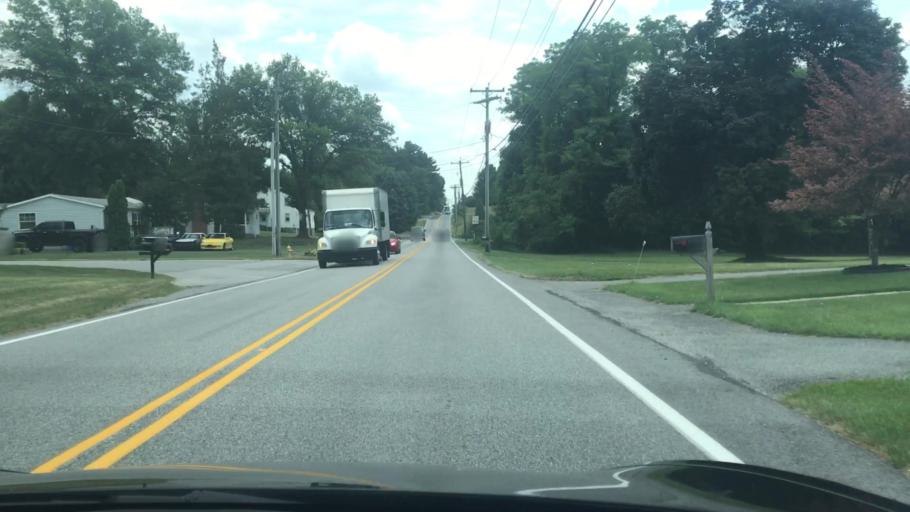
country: US
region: Pennsylvania
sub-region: York County
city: Emigsville
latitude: 40.0314
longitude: -76.7507
